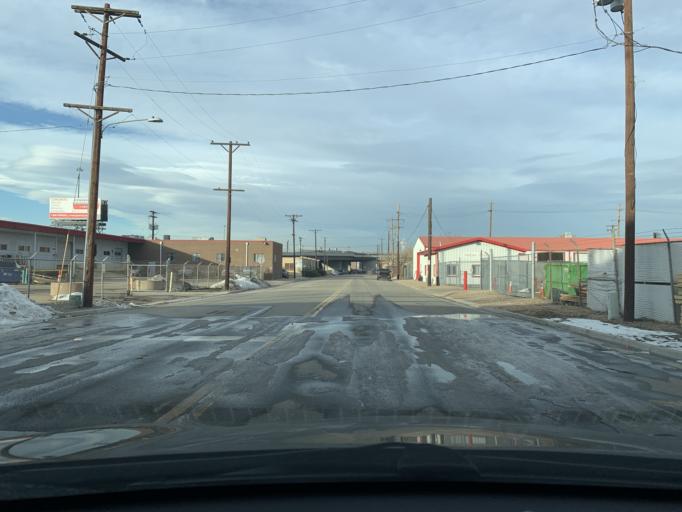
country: US
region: Colorado
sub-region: Denver County
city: Denver
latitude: 39.7376
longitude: -105.0123
